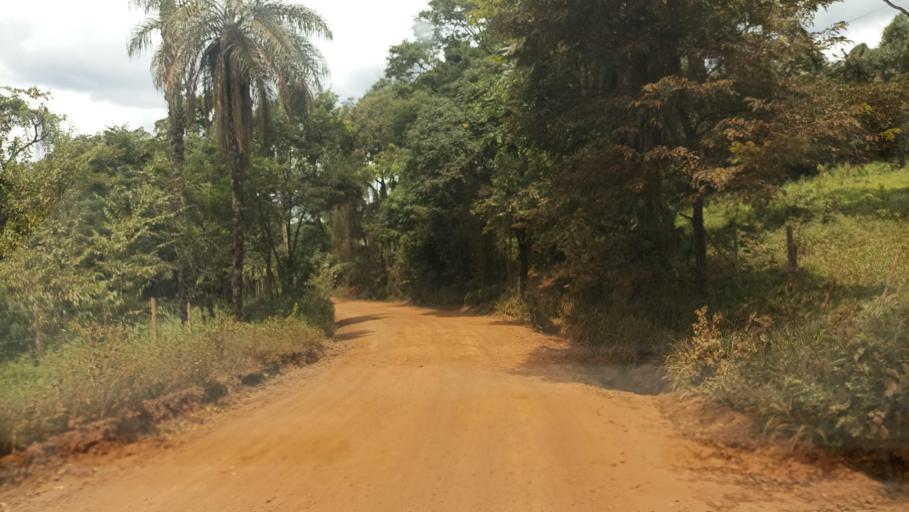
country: BR
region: Minas Gerais
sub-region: Itabirito
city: Itabirito
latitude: -20.3450
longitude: -43.7719
